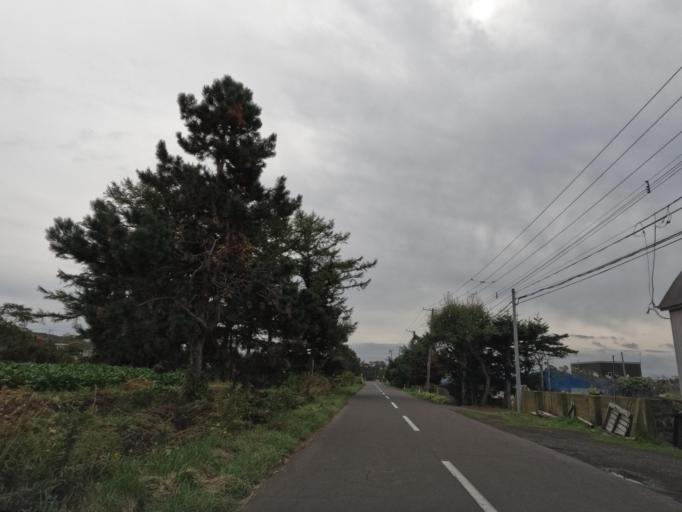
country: JP
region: Hokkaido
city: Date
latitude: 42.4318
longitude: 140.9101
